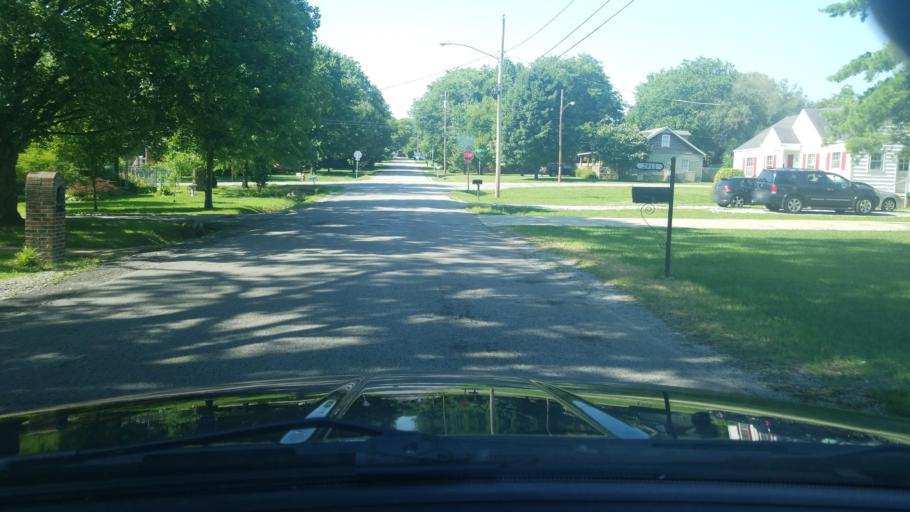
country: US
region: Tennessee
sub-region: Davidson County
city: Oak Hill
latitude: 36.1092
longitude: -86.7409
